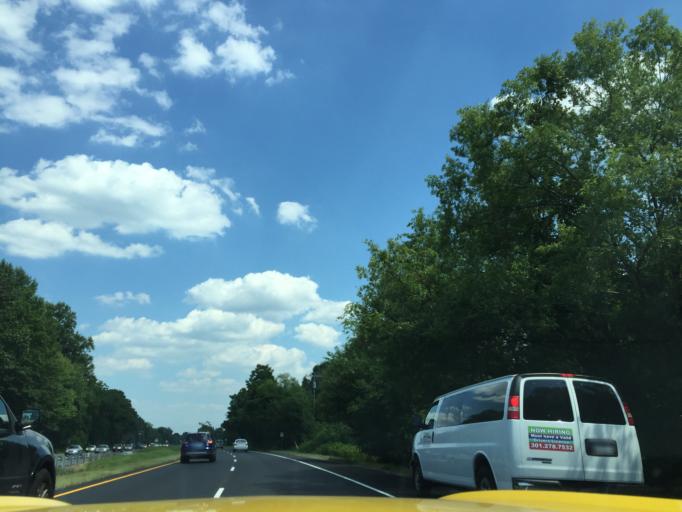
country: US
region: Virginia
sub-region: Fairfax County
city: Reston
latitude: 38.9771
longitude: -77.3142
